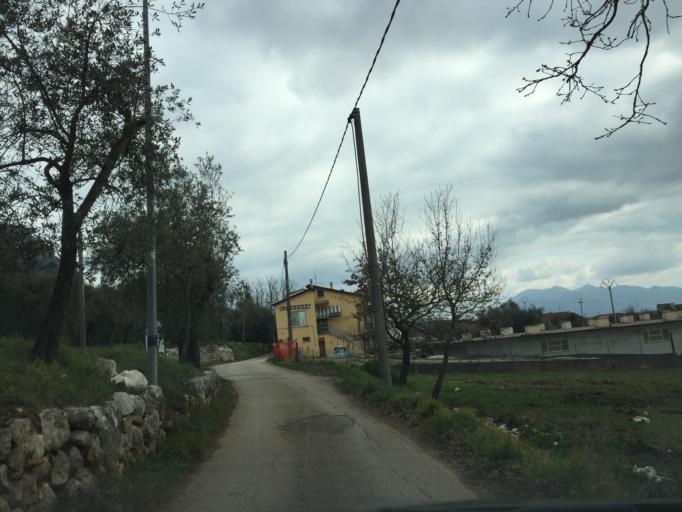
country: IT
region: Latium
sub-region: Provincia di Frosinone
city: Cassino
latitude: 41.4827
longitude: 13.8021
